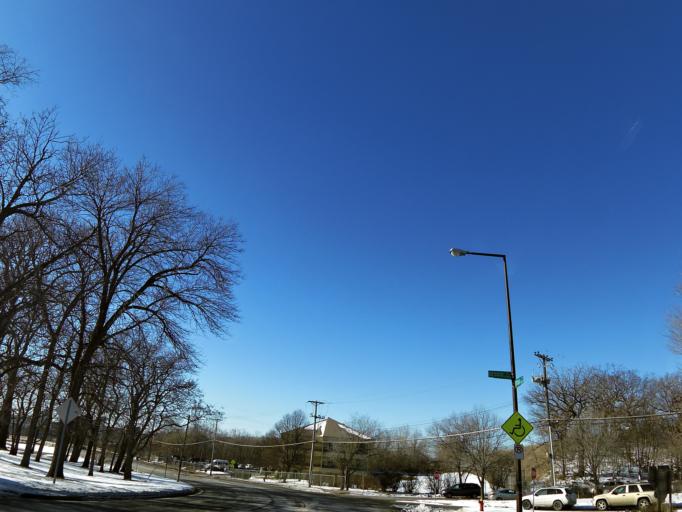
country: US
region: Minnesota
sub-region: Ramsey County
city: Saint Paul
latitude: 44.9601
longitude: -93.0809
